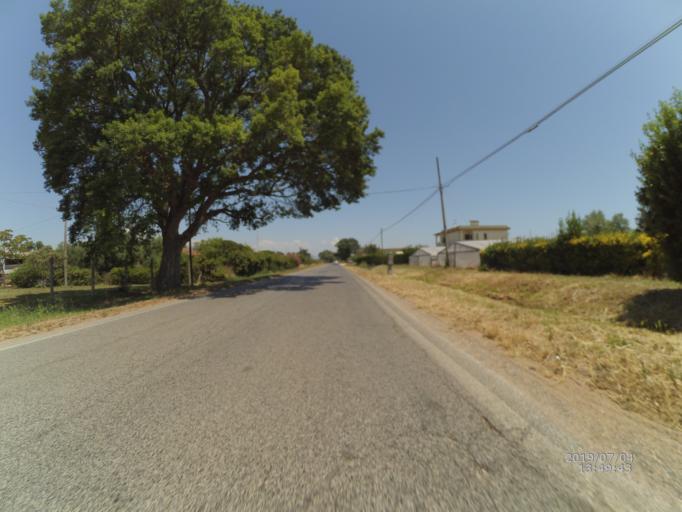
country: IT
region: Latium
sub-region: Provincia di Latina
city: San Felice Circeo
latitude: 41.2855
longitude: 13.1168
